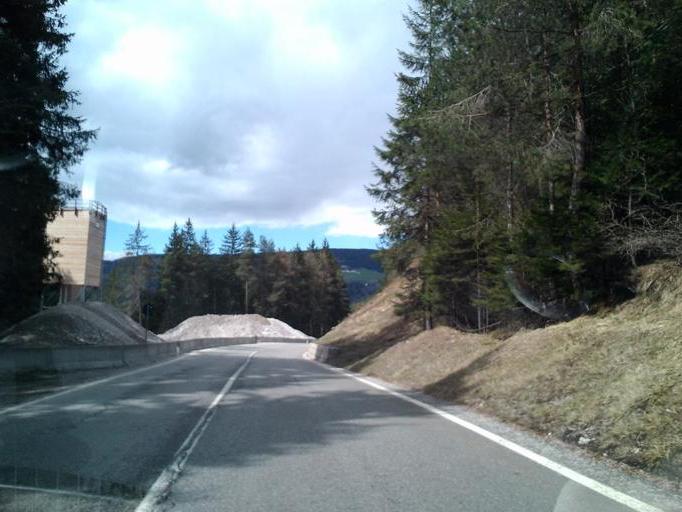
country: IT
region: Trentino-Alto Adige
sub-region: Bolzano
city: Dobbiaco
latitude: 46.7132
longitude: 12.2239
